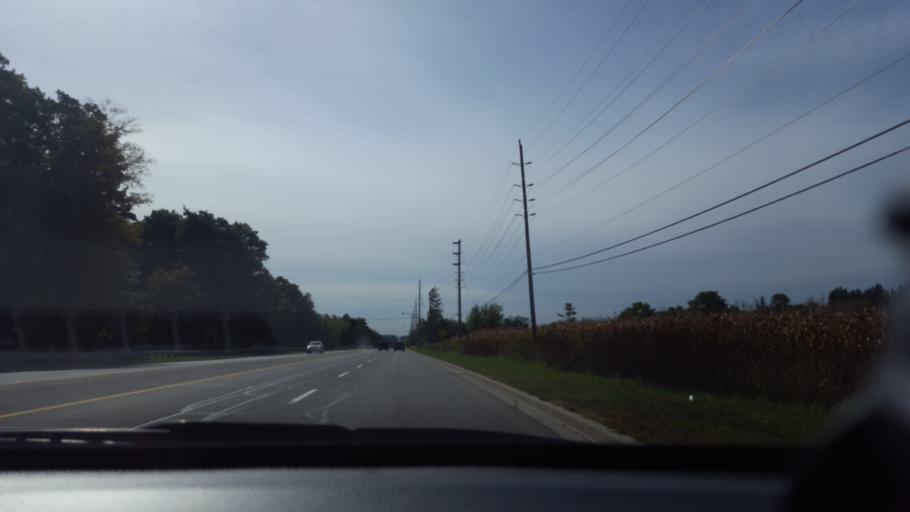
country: CA
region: Ontario
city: Newmarket
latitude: 44.0087
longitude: -79.4976
